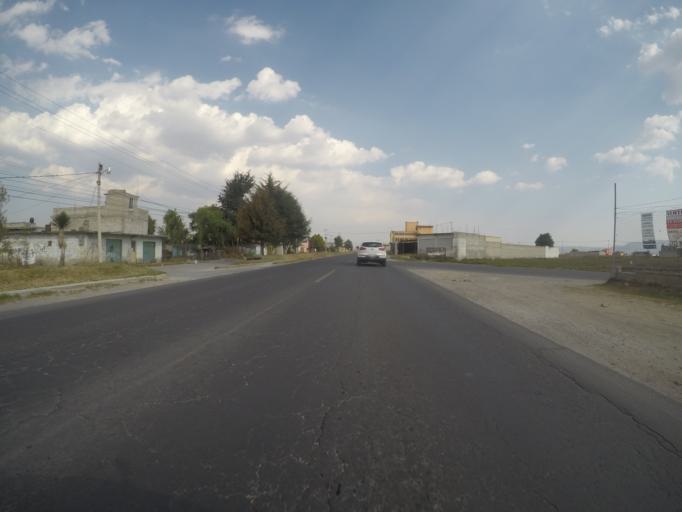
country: MX
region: Morelos
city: Chapultepec
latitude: 19.1997
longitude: -99.5464
